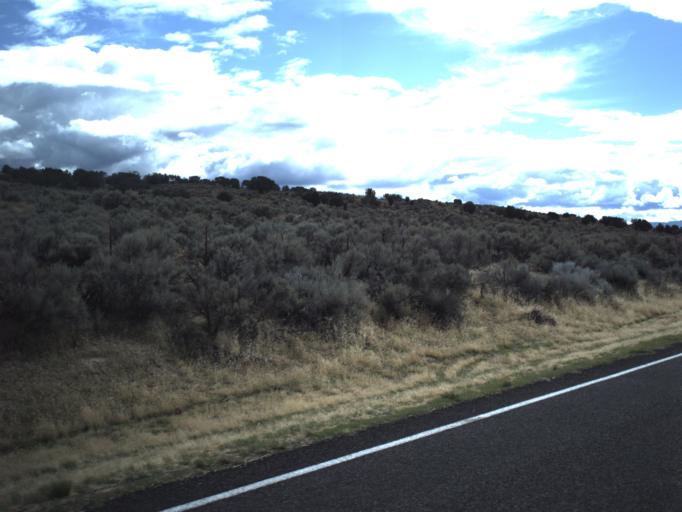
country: US
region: Utah
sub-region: Millard County
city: Fillmore
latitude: 39.0037
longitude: -112.4119
